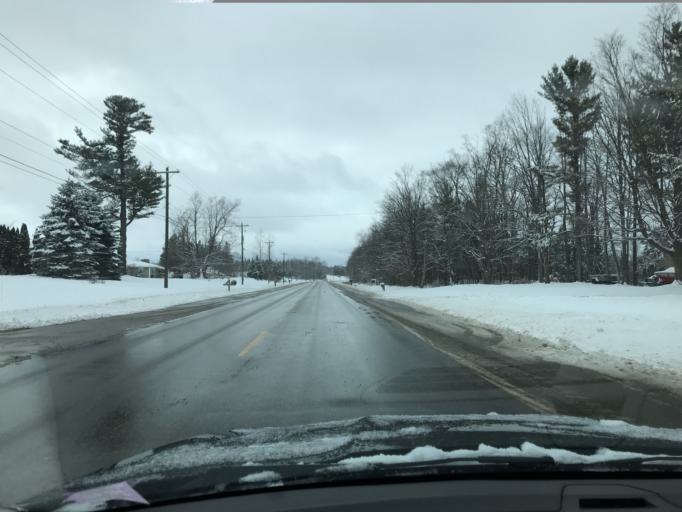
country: US
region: Michigan
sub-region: Charlevoix County
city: Charlevoix
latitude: 45.2803
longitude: -85.2331
